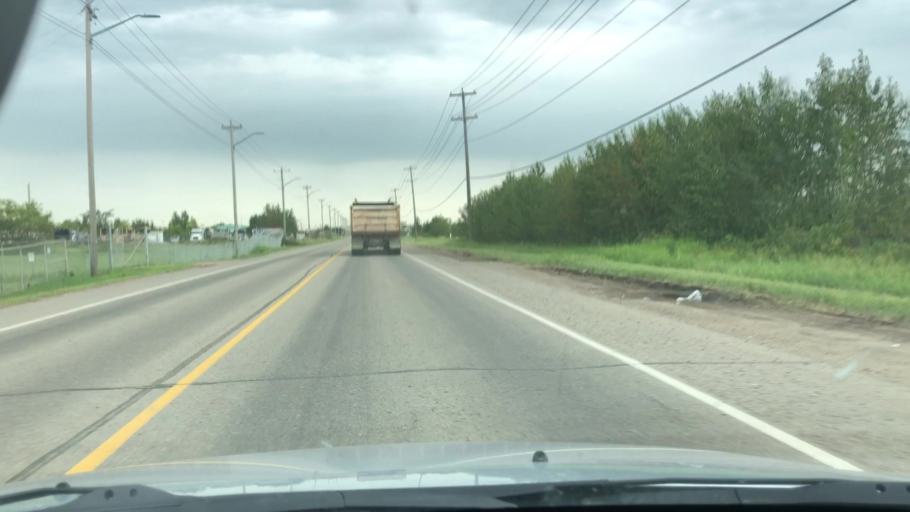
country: CA
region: Alberta
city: Sherwood Park
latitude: 53.5248
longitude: -113.3939
